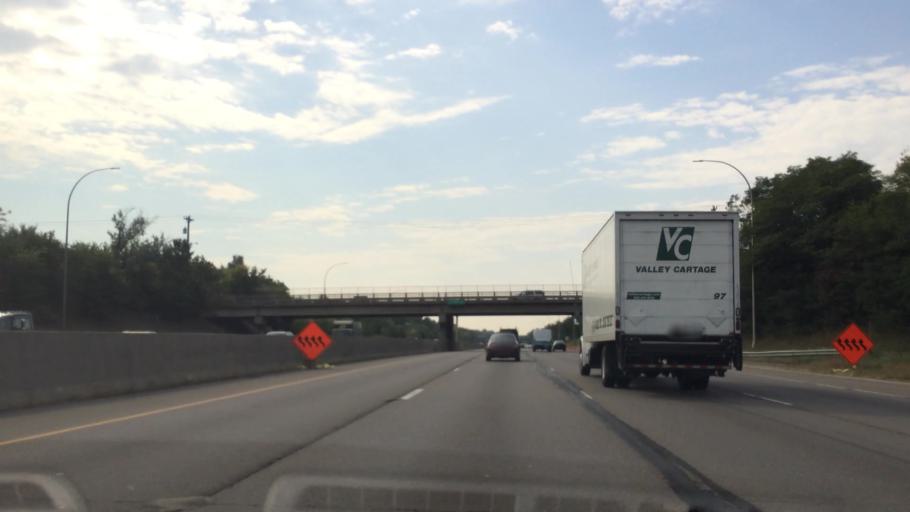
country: US
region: Minnesota
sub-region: Hennepin County
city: Minneapolis
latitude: 44.9351
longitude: -93.2748
